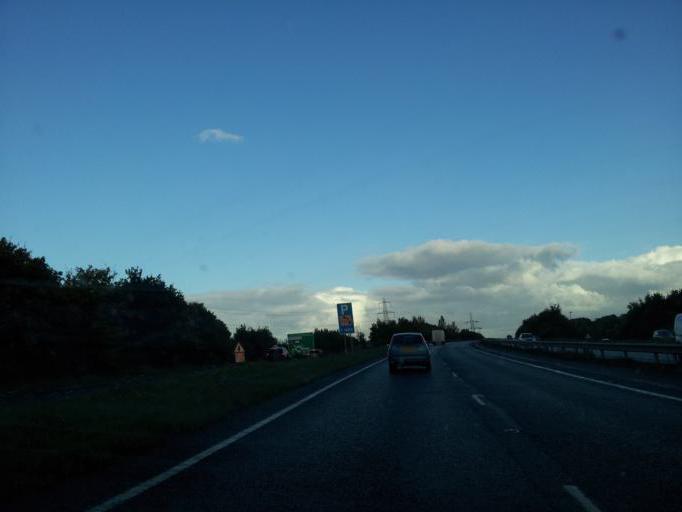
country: GB
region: England
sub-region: Norfolk
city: Cringleford
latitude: 52.6009
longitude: 1.2266
